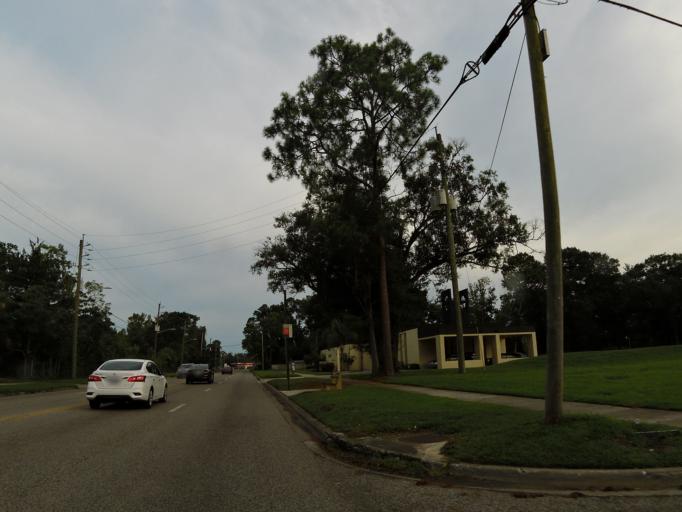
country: US
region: Florida
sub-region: Duval County
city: Jacksonville
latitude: 30.3752
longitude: -81.6903
